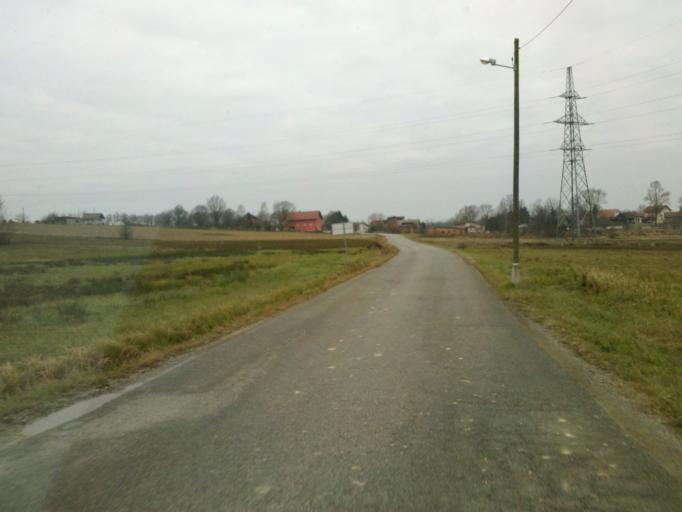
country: HR
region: Grad Zagreb
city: Horvati
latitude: 45.6846
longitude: 15.8574
